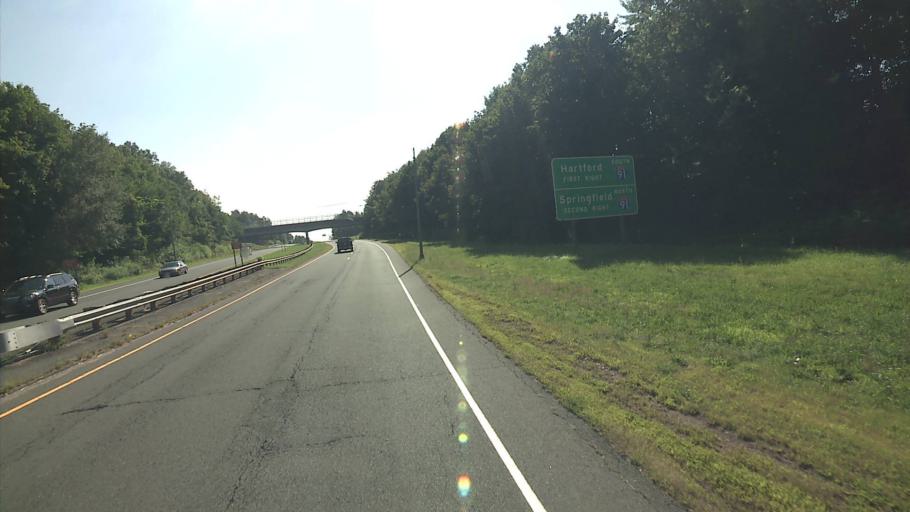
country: US
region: Connecticut
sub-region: Hartford County
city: Thompsonville
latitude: 41.9904
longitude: -72.5963
